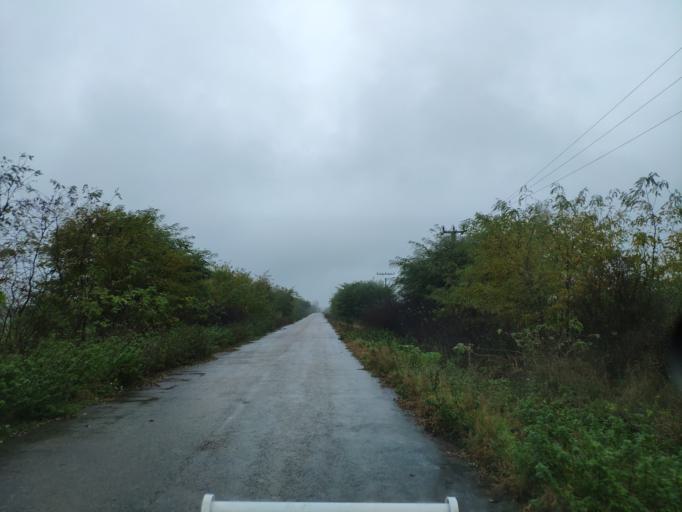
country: SK
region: Kosicky
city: Cierna nad Tisou
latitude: 48.4320
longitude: 22.0023
